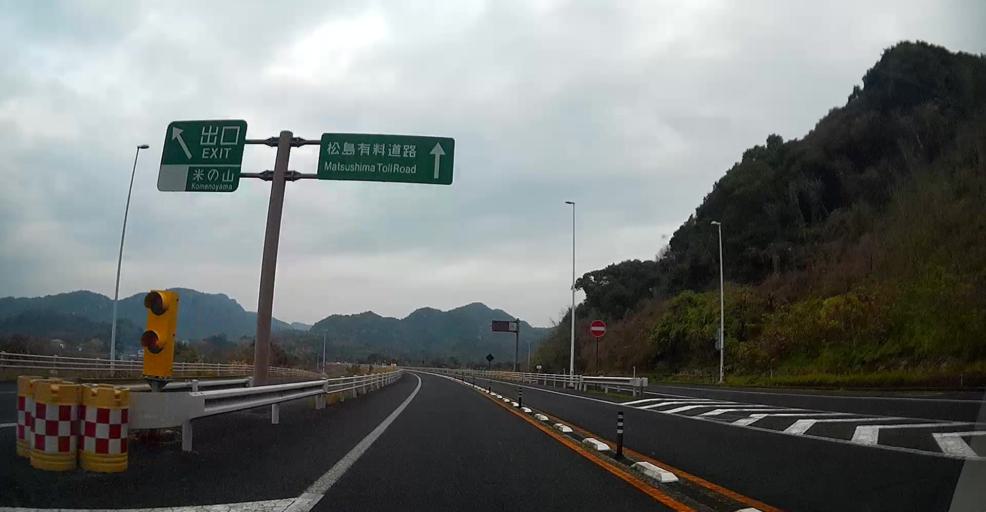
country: JP
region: Kumamoto
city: Hondo
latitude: 32.4969
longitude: 130.3890
